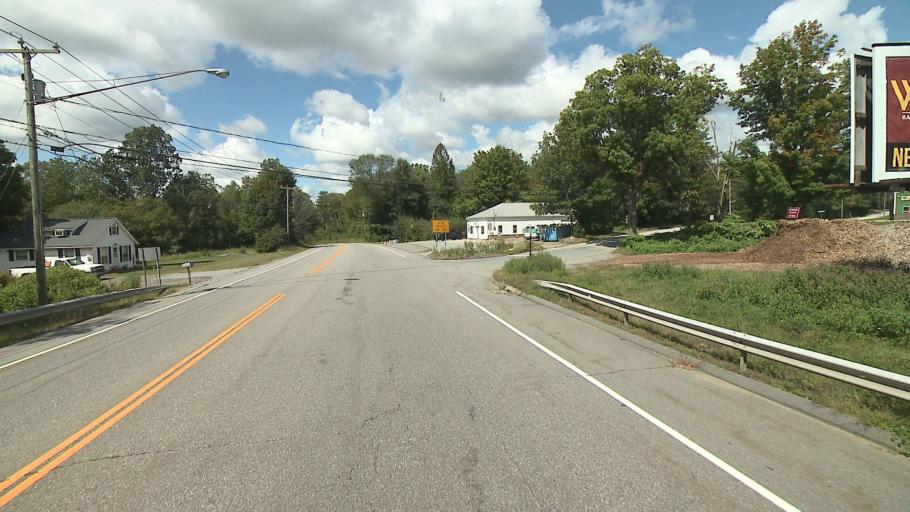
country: US
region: Connecticut
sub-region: Windham County
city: South Woodstock
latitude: 41.8783
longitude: -72.0916
